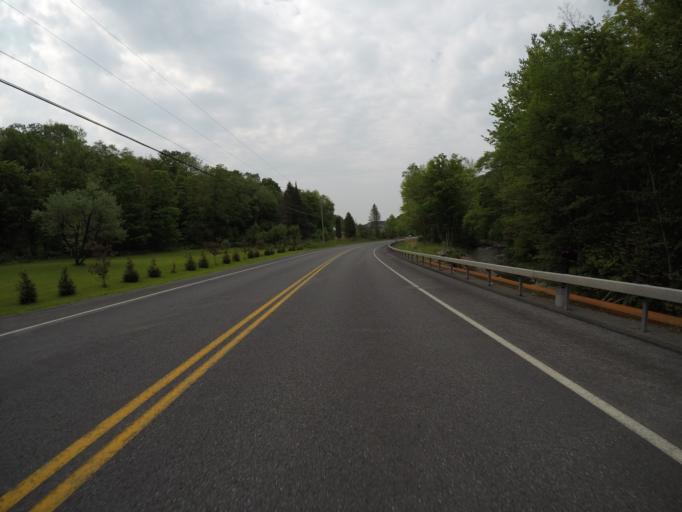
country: US
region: New York
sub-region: Sullivan County
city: Livingston Manor
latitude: 42.0135
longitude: -74.8905
